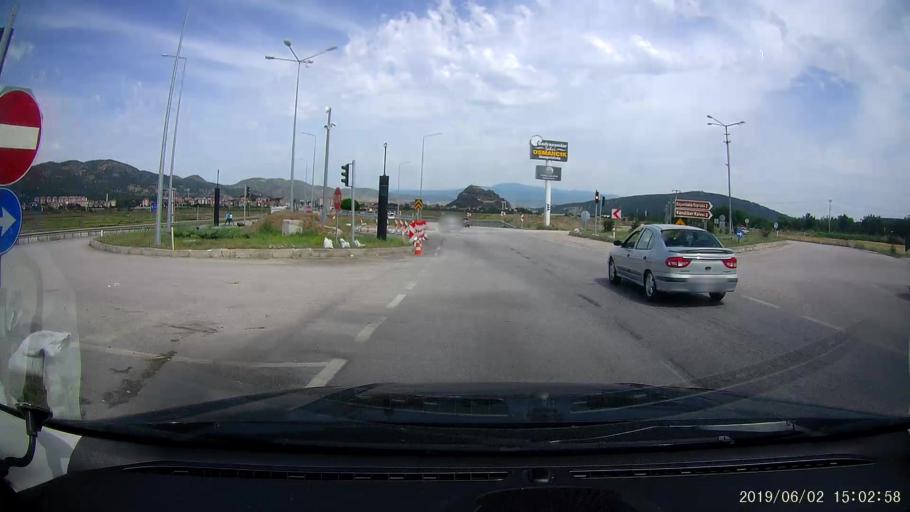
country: TR
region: Corum
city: Osmancik
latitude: 40.9776
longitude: 34.7740
